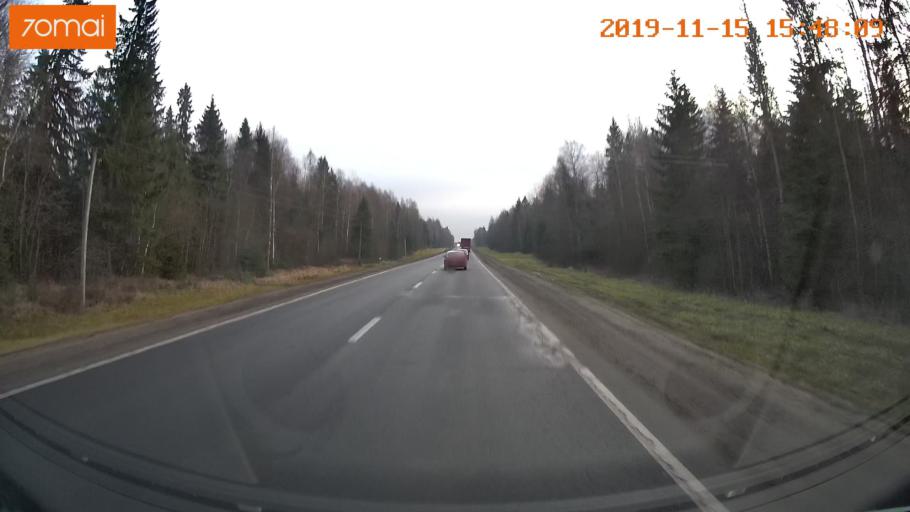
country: RU
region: Jaroslavl
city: Danilov
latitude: 57.9305
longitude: 40.0065
